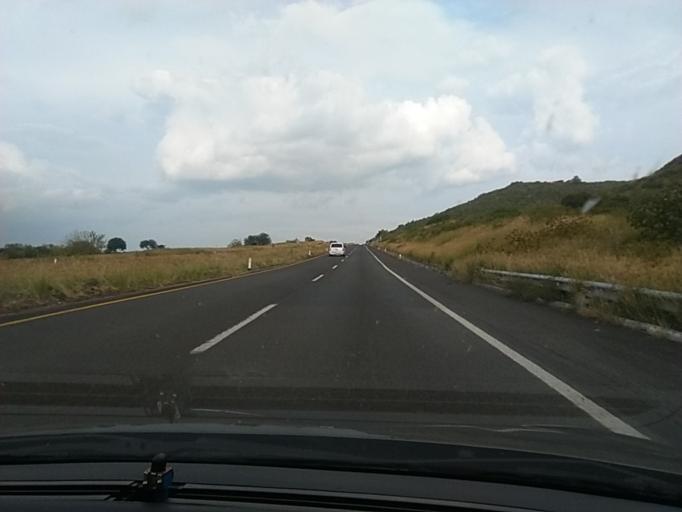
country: MX
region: Mexico
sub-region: Chapultepec
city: Chucandiro
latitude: 19.9039
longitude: -101.2862
